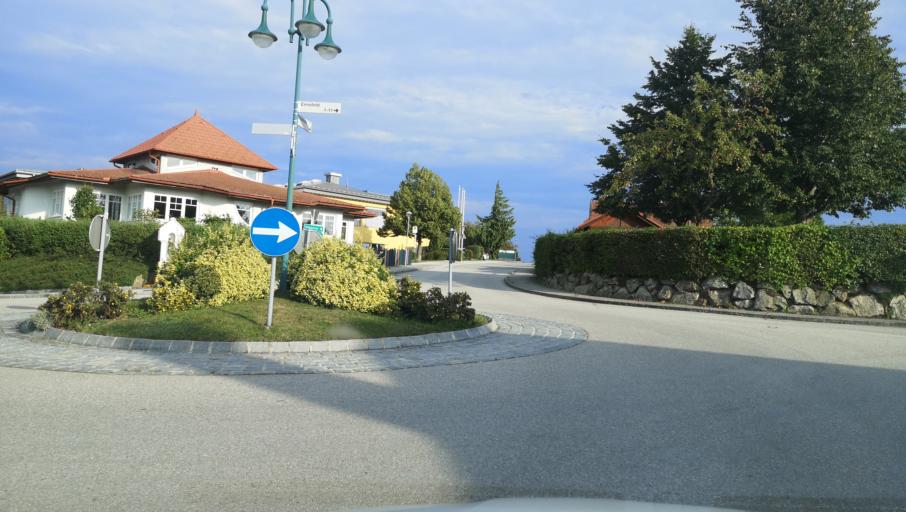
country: AT
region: Lower Austria
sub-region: Politischer Bezirk Amstetten
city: Amstetten
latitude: 48.1499
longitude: 14.8898
